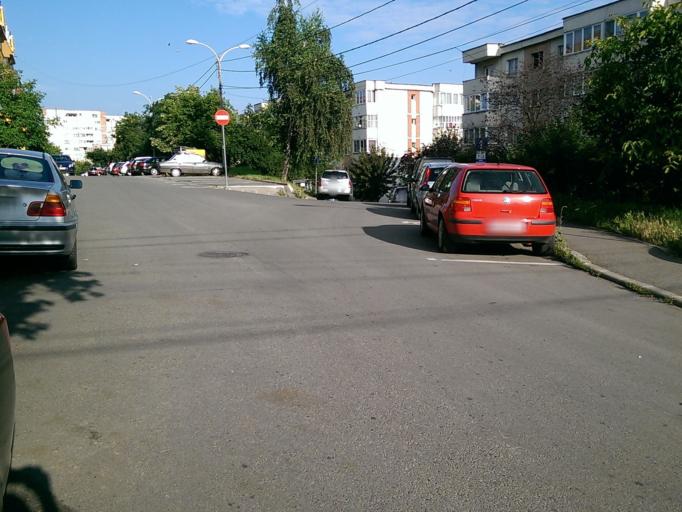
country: RO
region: Cluj
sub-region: Municipiul Cluj-Napoca
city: Cluj-Napoca
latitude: 46.7689
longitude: 23.6129
